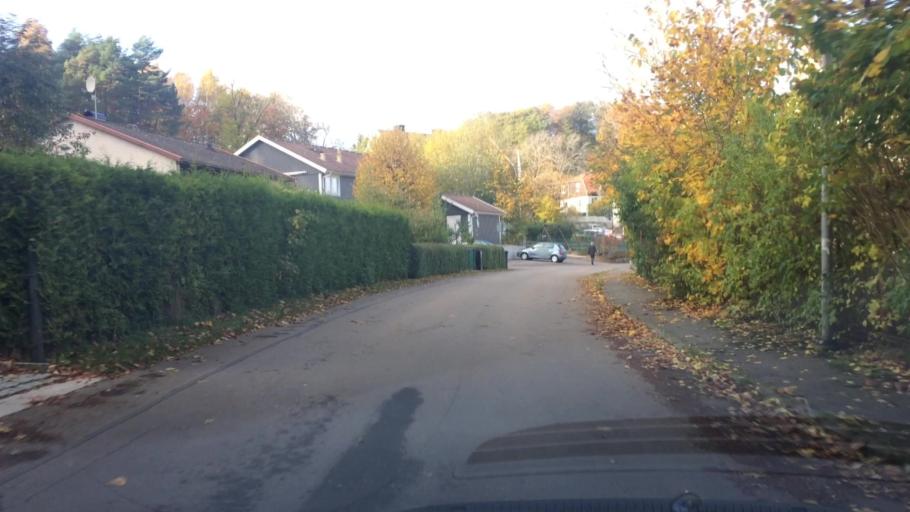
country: SE
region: Vaestra Goetaland
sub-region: Molndal
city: Moelndal
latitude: 57.6520
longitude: 12.0098
